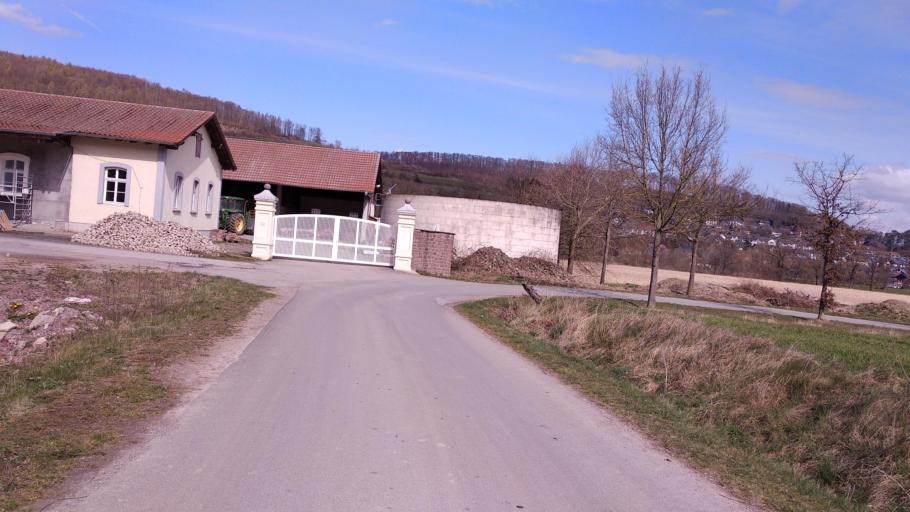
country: DE
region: North Rhine-Westphalia
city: Beverungen
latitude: 51.6565
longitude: 9.3562
